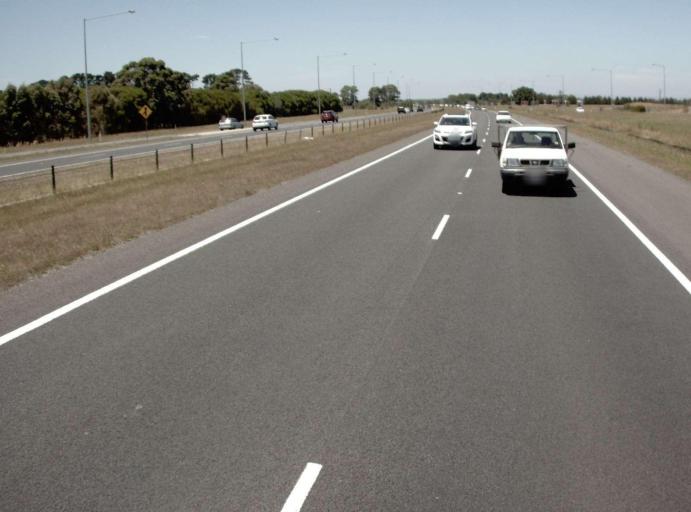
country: AU
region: Victoria
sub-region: Cardinia
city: Officer South
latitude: -38.0718
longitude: 145.3888
